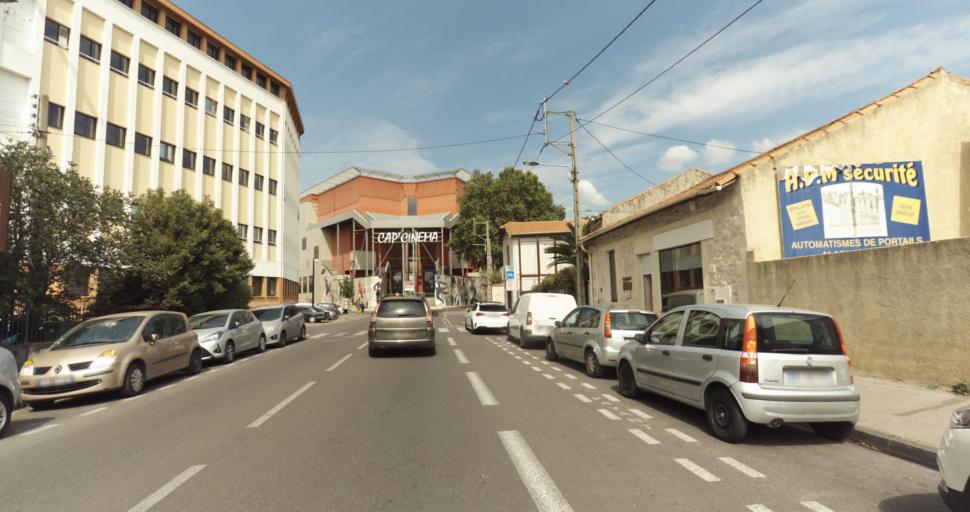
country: FR
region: Languedoc-Roussillon
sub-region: Departement du Gard
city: Nimes
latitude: 43.8304
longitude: 4.3698
